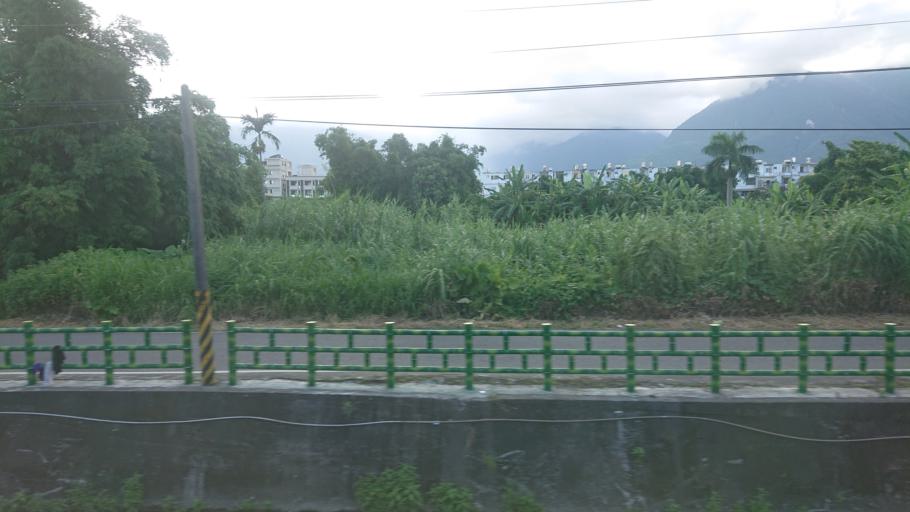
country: TW
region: Taiwan
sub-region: Hualien
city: Hualian
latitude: 23.9812
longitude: 121.5952
